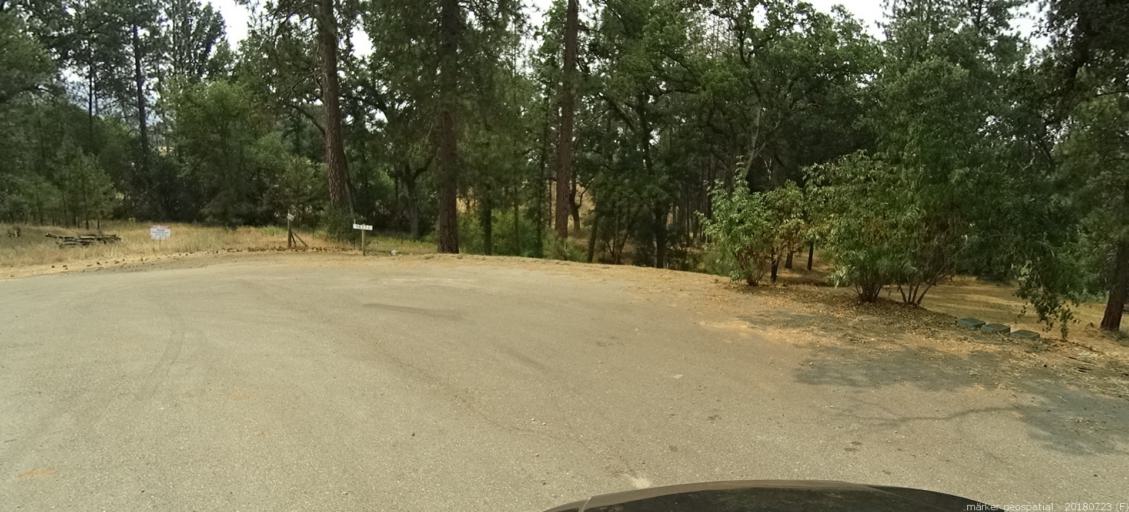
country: US
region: California
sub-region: Madera County
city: Oakhurst
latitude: 37.3300
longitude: -119.6659
